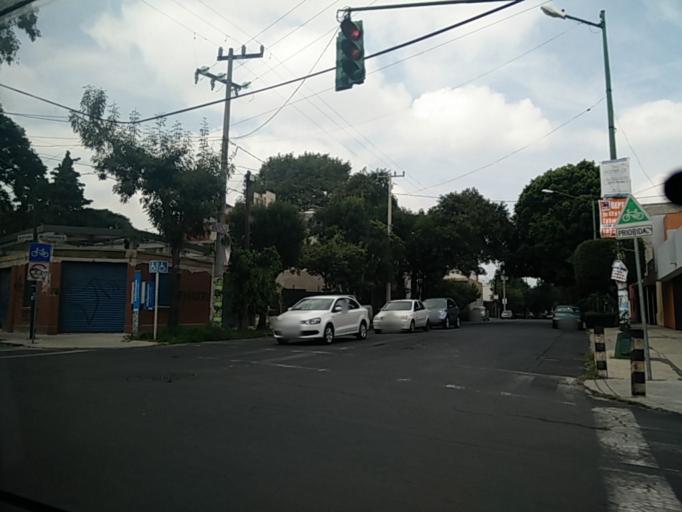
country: MX
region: Mexico City
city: Coyoacan
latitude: 19.3548
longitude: -99.1634
